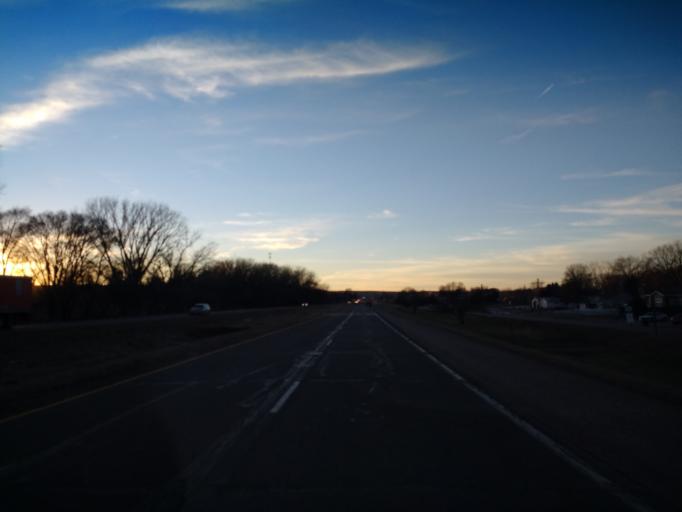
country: US
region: Iowa
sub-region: Woodbury County
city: Moville
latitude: 42.4819
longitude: -96.0688
